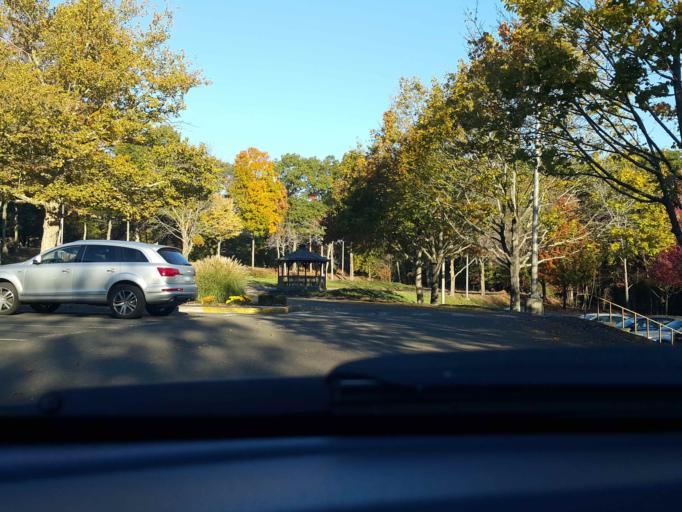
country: US
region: Connecticut
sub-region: New Haven County
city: Seymour
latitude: 41.3918
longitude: -73.0501
